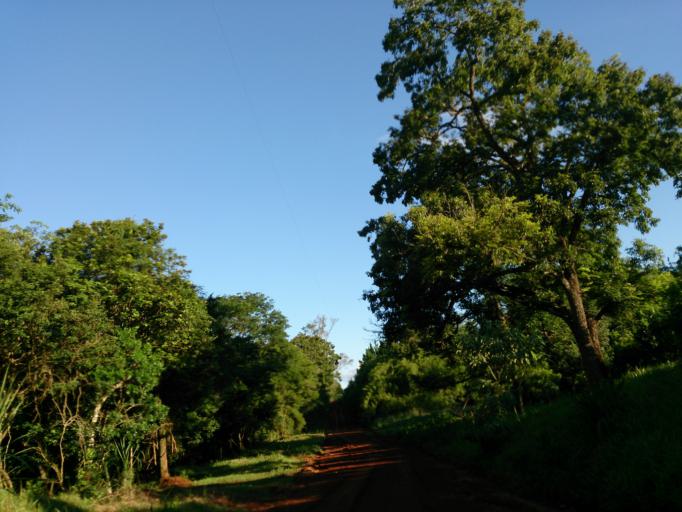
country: AR
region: Misiones
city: Guarani
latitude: -27.5599
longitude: -55.1774
